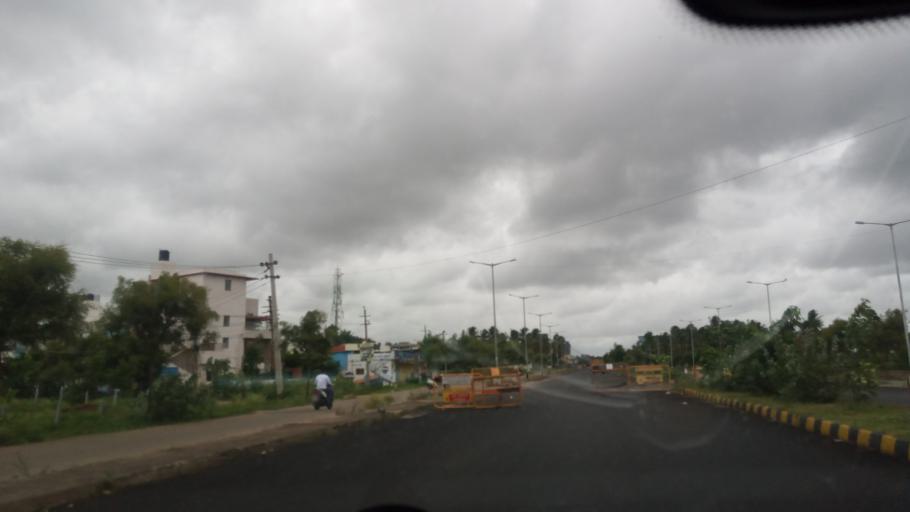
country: IN
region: Karnataka
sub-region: Mysore
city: Mysore
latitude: 12.2914
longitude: 76.6054
